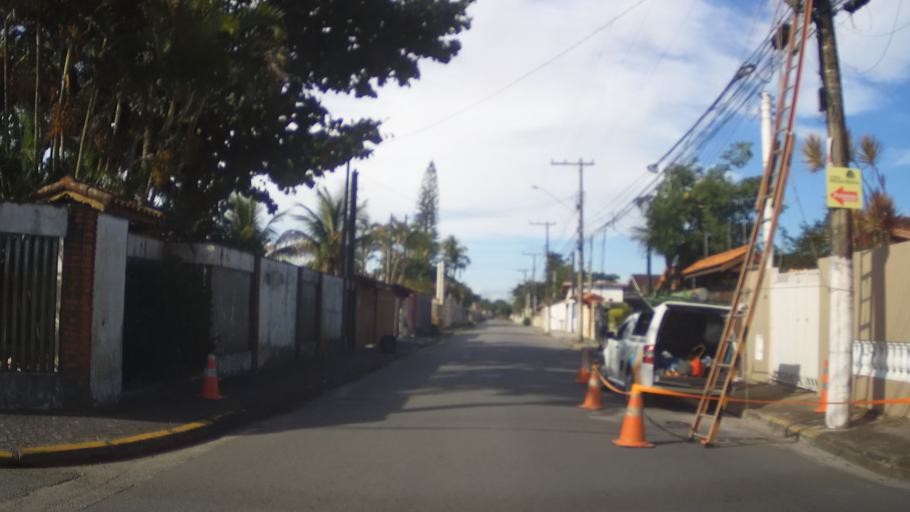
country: BR
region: Sao Paulo
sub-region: Itanhaem
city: Itanhaem
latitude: -24.1657
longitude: -46.7540
